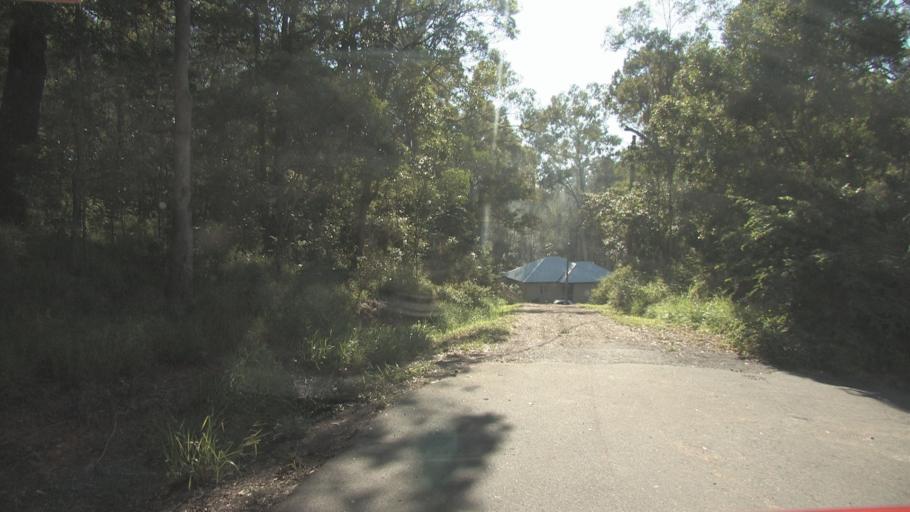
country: AU
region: Queensland
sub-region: Gold Coast
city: Yatala
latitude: -27.6882
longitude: 153.2682
